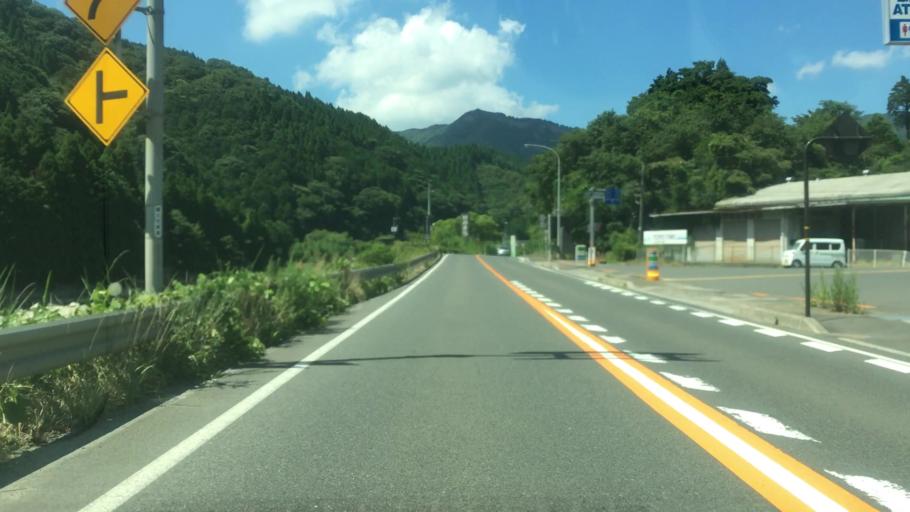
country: JP
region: Tottori
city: Tottori
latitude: 35.2733
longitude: 134.2240
